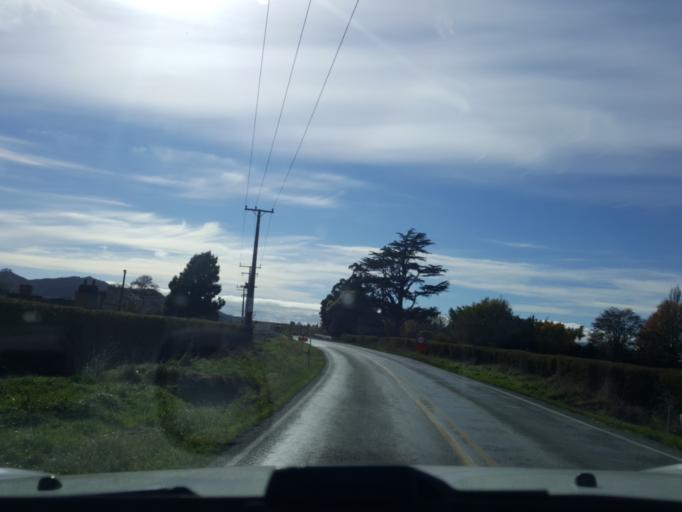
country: NZ
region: Waikato
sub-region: Waikato District
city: Ngaruawahia
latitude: -37.6014
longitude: 175.2019
